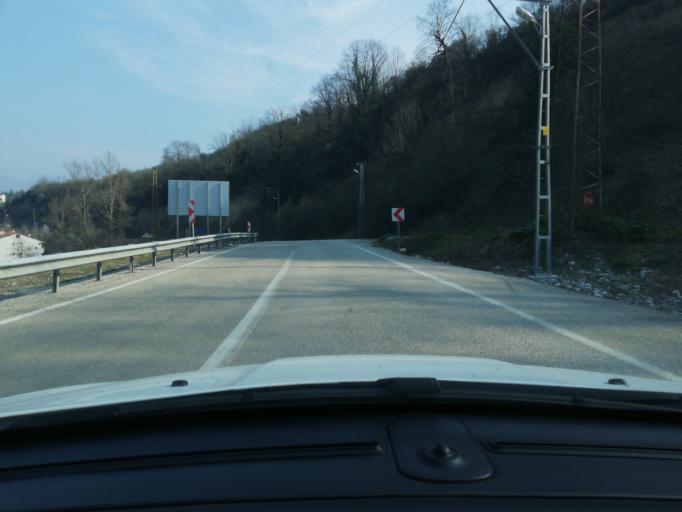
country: TR
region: Karabuk
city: Yenice
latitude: 41.2076
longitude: 32.3672
